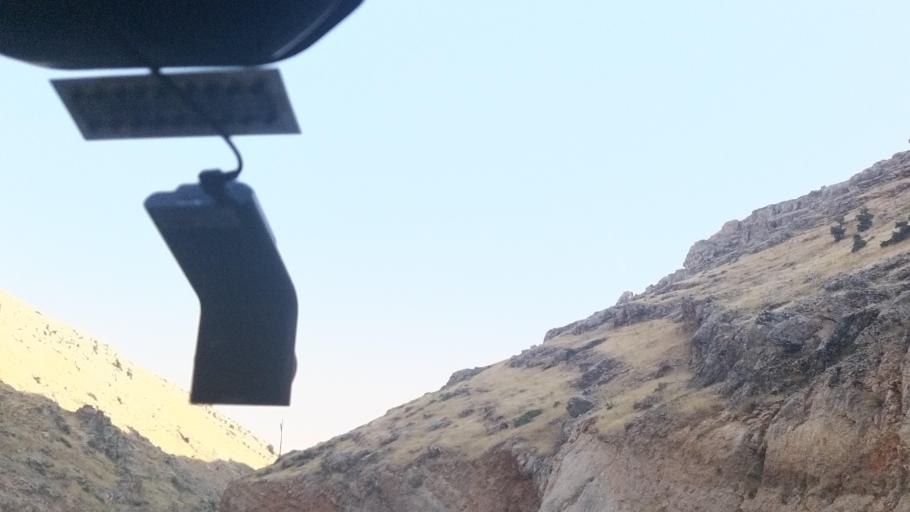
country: TR
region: Diyarbakir
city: Silvan
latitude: 38.1639
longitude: 41.0012
